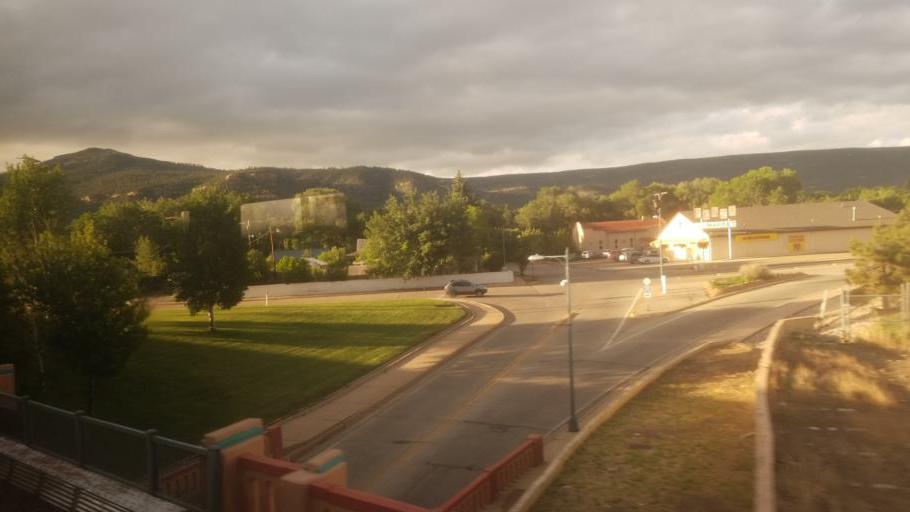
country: US
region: New Mexico
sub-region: Colfax County
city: Raton
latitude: 36.9045
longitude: -104.4384
